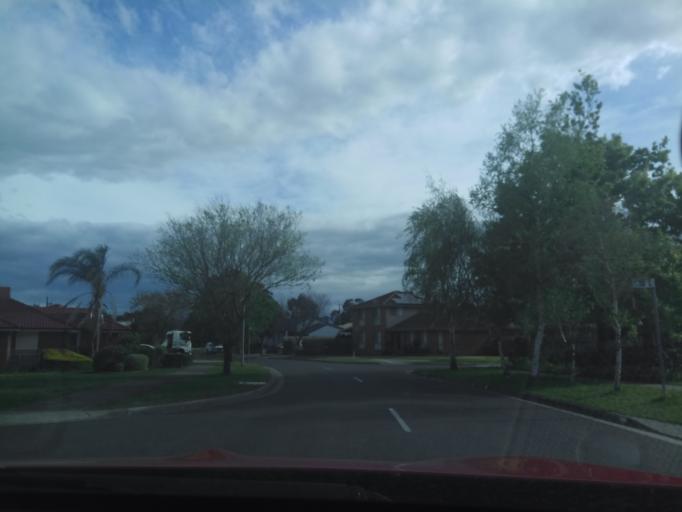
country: AU
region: Victoria
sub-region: Casey
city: Cranbourne North
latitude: -38.0736
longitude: 145.2756
